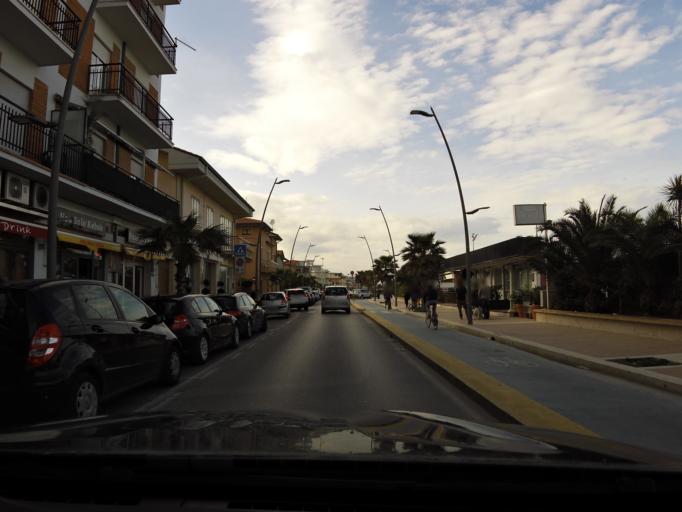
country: IT
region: The Marches
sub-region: Provincia di Macerata
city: Civitanova Marche
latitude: 43.3154
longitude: 13.7242
